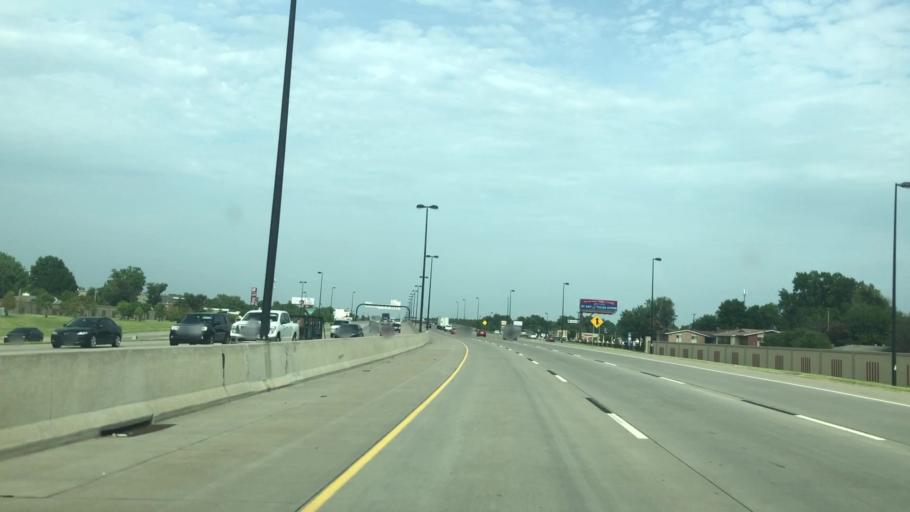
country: US
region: Oklahoma
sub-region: Tulsa County
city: Tulsa
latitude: 36.0896
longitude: -95.9810
